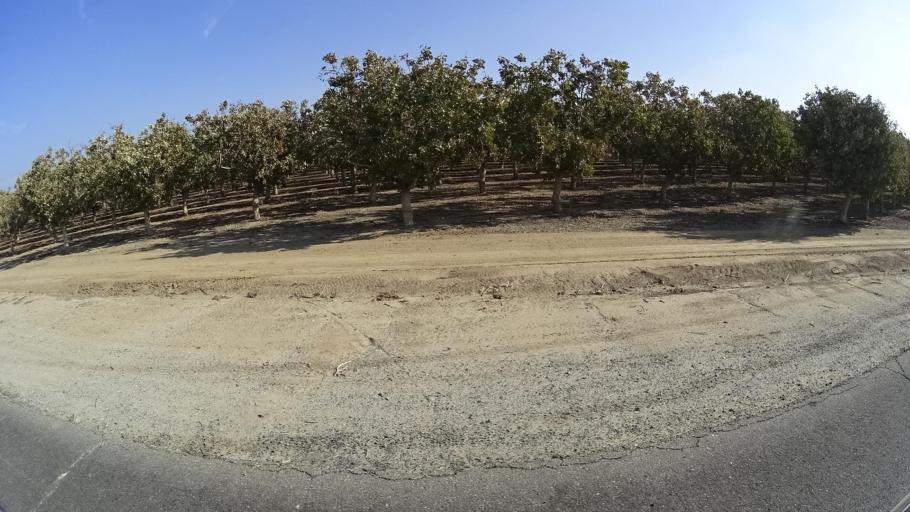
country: US
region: California
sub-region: Kern County
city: McFarland
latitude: 35.6594
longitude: -119.1953
